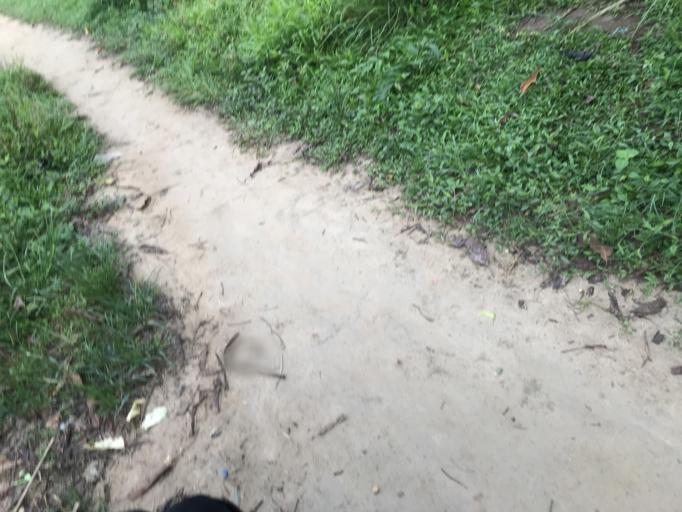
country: SL
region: Eastern Province
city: Pendembu
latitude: 8.0937
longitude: -10.6967
